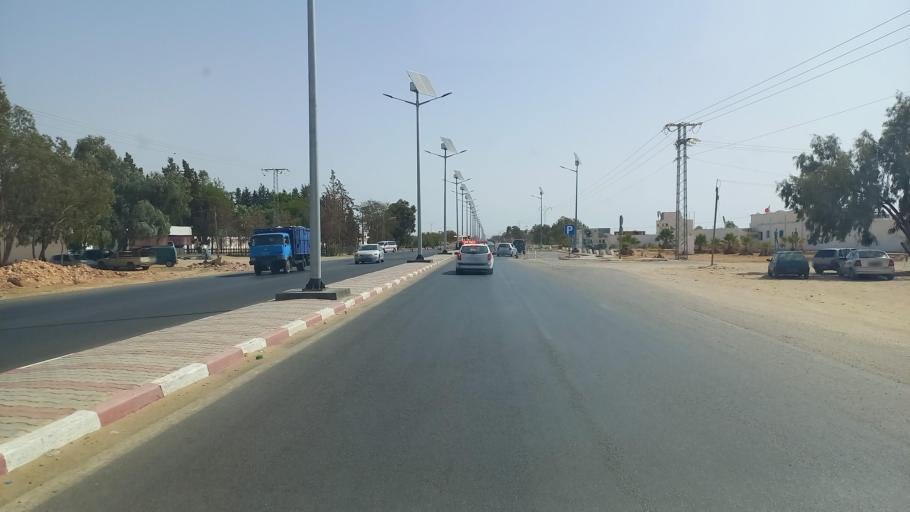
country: TN
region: Madanin
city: Medenine
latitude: 33.3522
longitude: 10.5337
